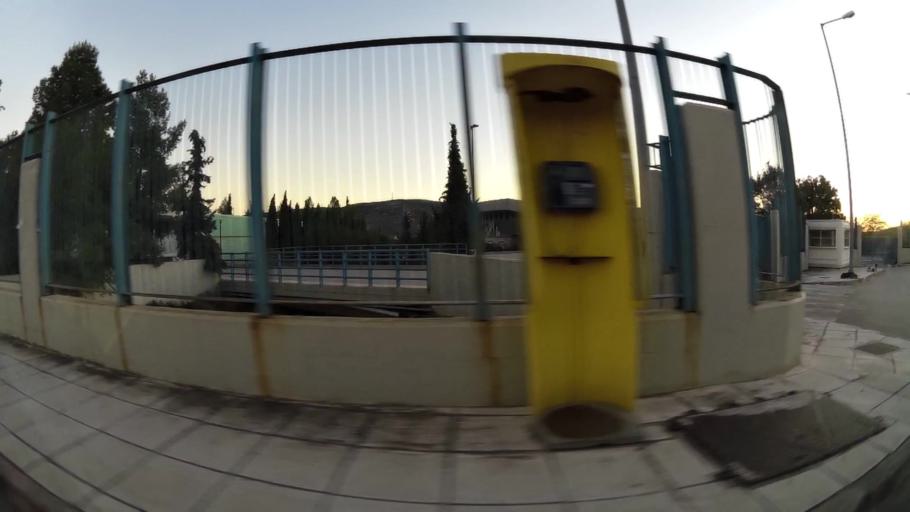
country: GR
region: Attica
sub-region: Nomarchia Dytikis Attikis
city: Ano Liosia
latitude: 38.0835
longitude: 23.6877
